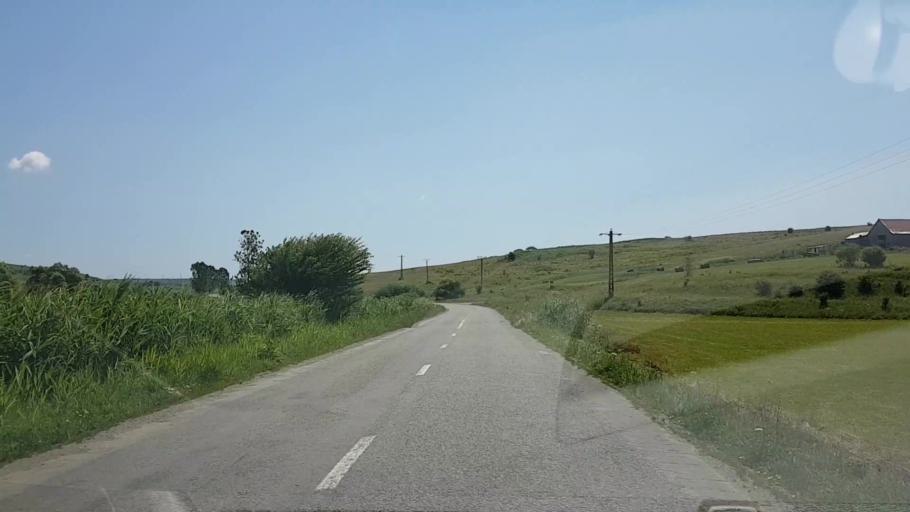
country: RO
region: Sibiu
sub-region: Comuna Merghindeal
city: Merghindeal
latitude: 45.9617
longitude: 24.7422
